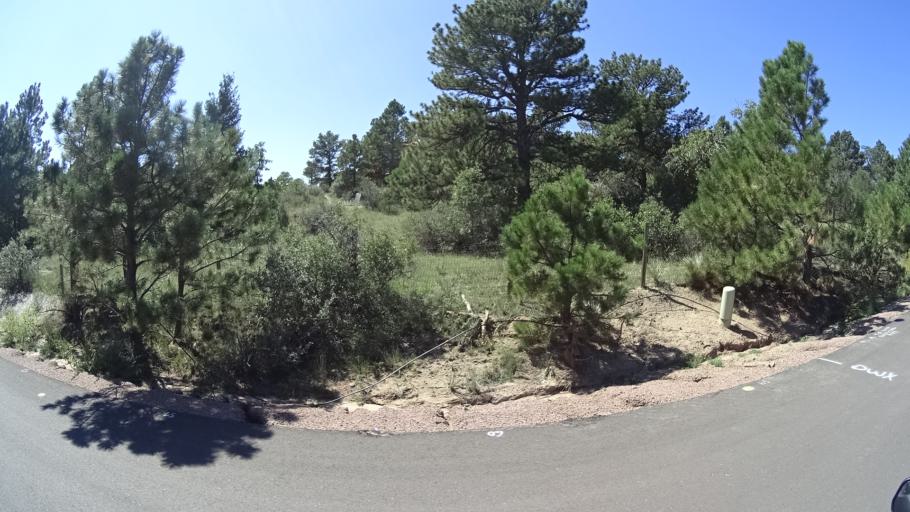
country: US
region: Colorado
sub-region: El Paso County
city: Cimarron Hills
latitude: 38.8625
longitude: -104.7389
